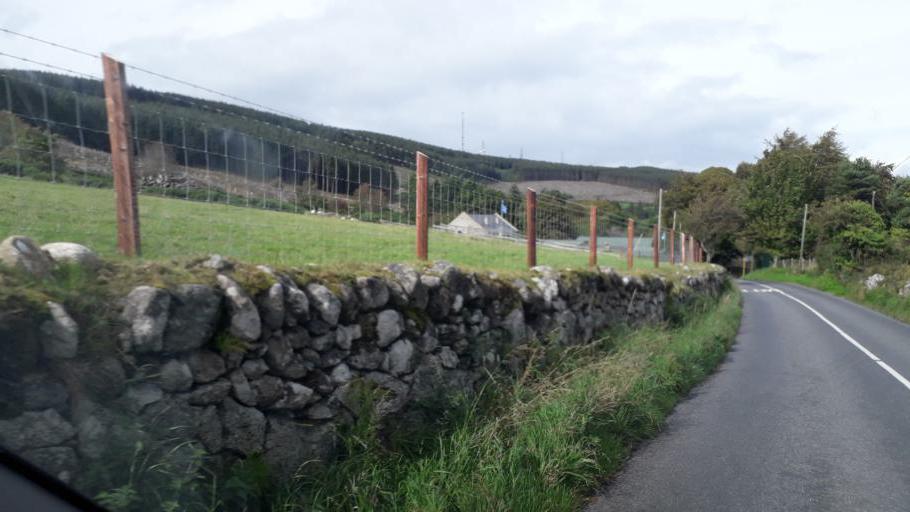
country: IE
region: Leinster
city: Sandyford
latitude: 53.2317
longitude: -6.2211
